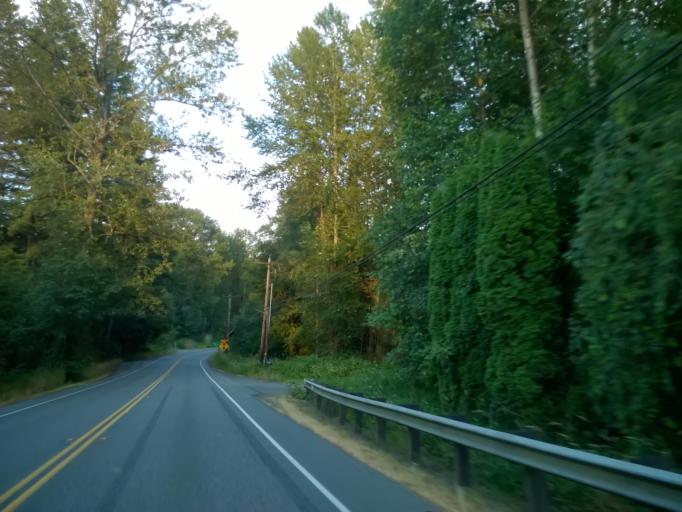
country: US
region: Washington
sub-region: King County
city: Cottage Lake
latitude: 47.7549
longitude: -122.0566
